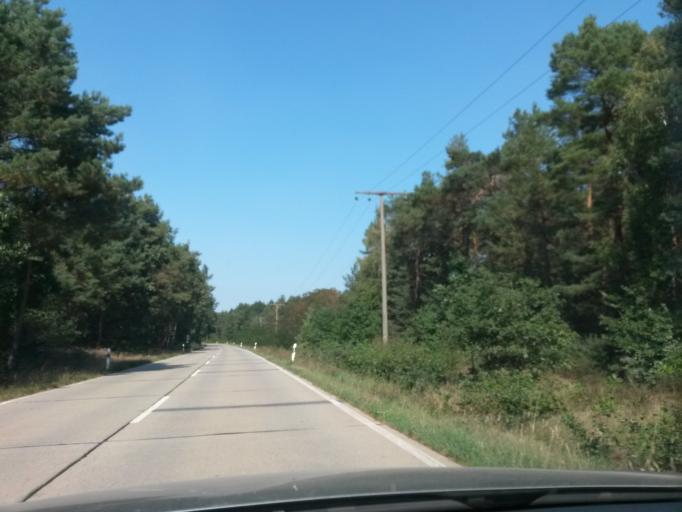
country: DE
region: Saxony-Anhalt
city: Jerichow
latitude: 52.4829
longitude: 12.0346
